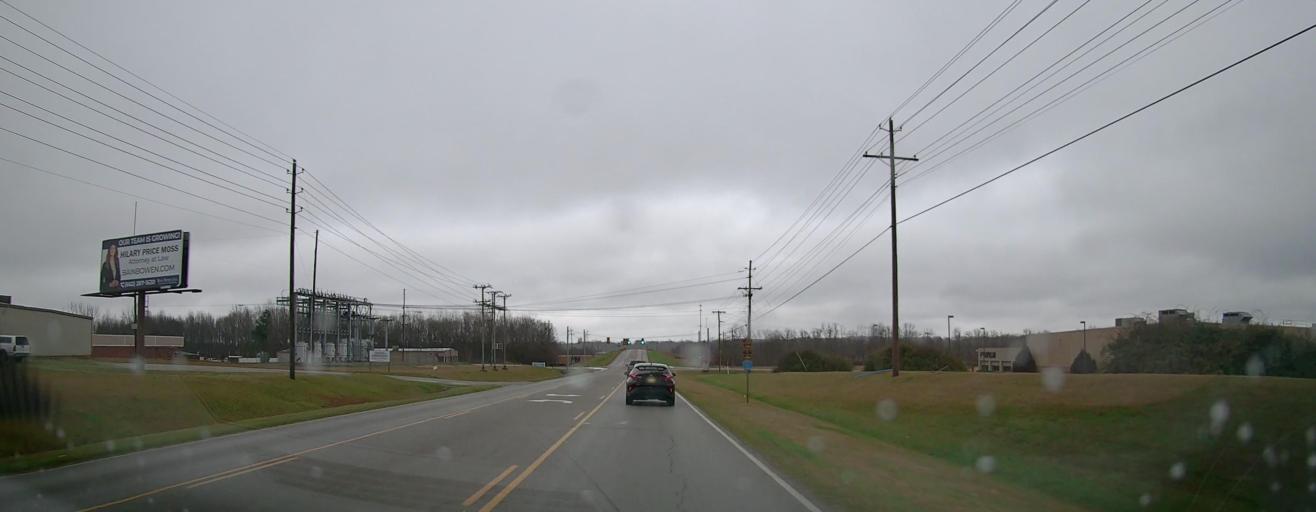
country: US
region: Mississippi
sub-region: Alcorn County
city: Corinth
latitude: 34.9091
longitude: -88.5190
